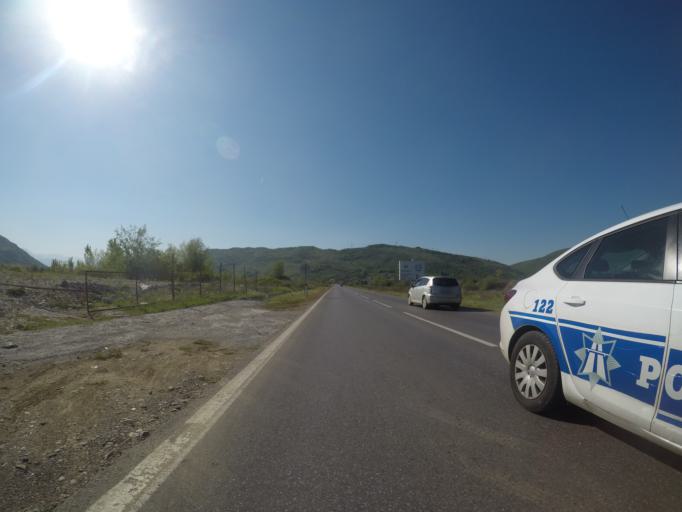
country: ME
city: Spuz
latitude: 42.4681
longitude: 19.1744
